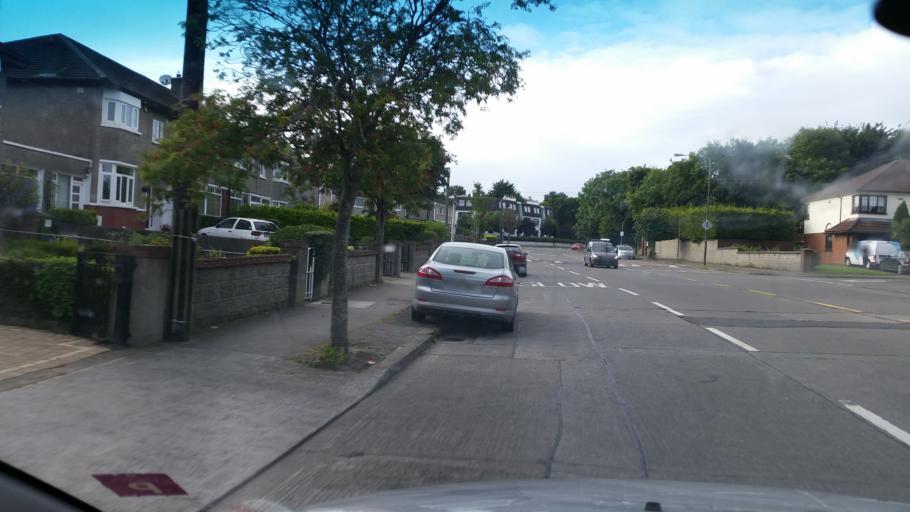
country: IE
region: Leinster
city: Glasnevin
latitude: 53.3839
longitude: -6.2768
